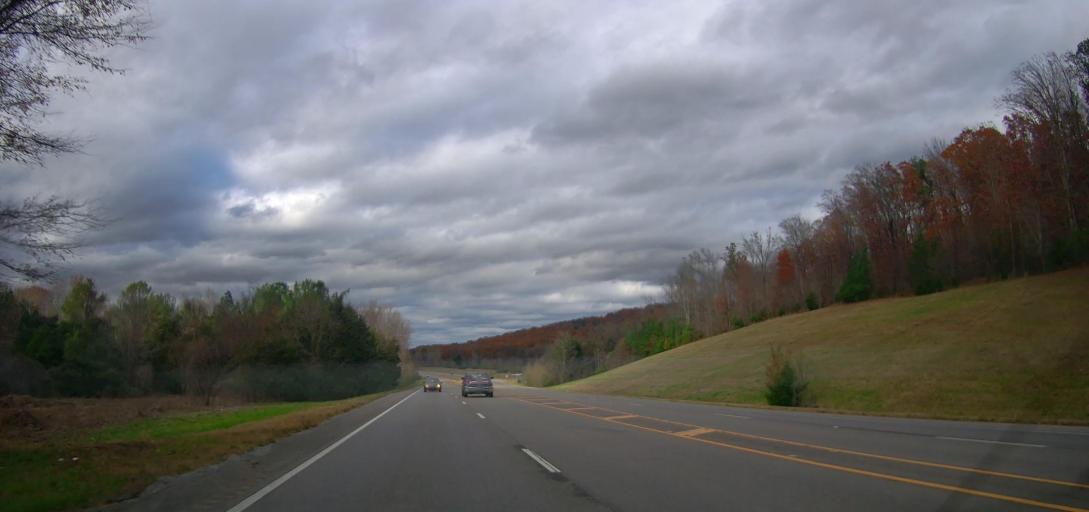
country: US
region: Alabama
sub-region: Morgan County
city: Falkville
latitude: 34.3209
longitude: -87.0007
